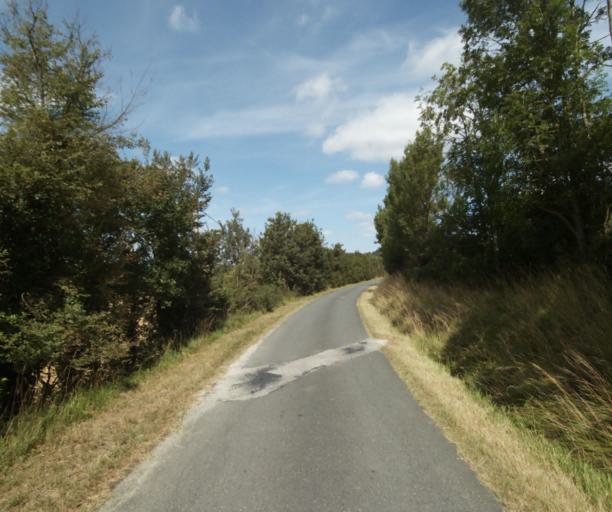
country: FR
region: Midi-Pyrenees
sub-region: Departement du Tarn
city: Dourgne
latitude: 43.4800
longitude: 2.1076
